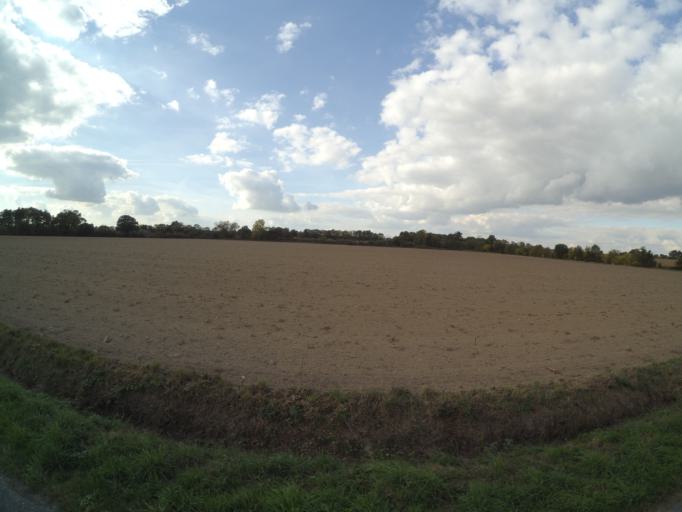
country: FR
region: Pays de la Loire
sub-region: Departement de la Loire-Atlantique
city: Saint-Lumine-de-Clisson
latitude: 47.0631
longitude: -1.3347
